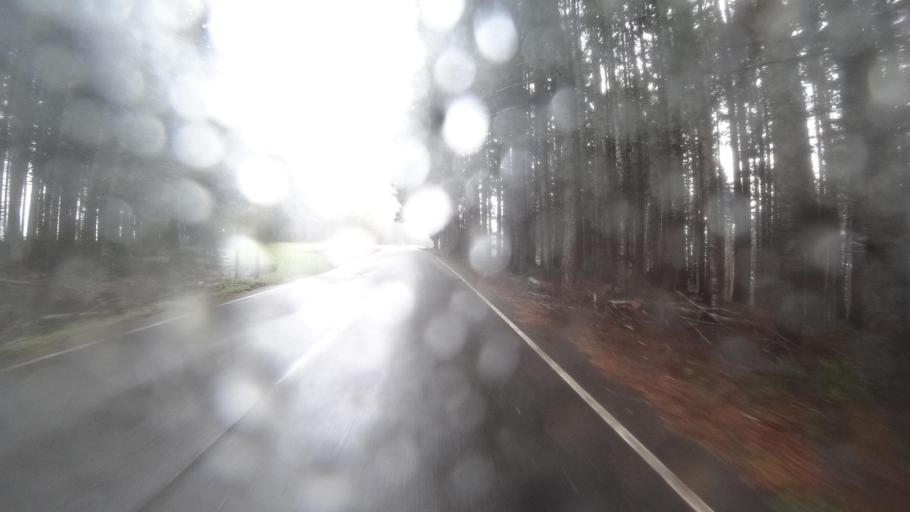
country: US
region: California
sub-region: Humboldt County
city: Westhaven-Moonstone
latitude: 41.2047
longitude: -123.9492
